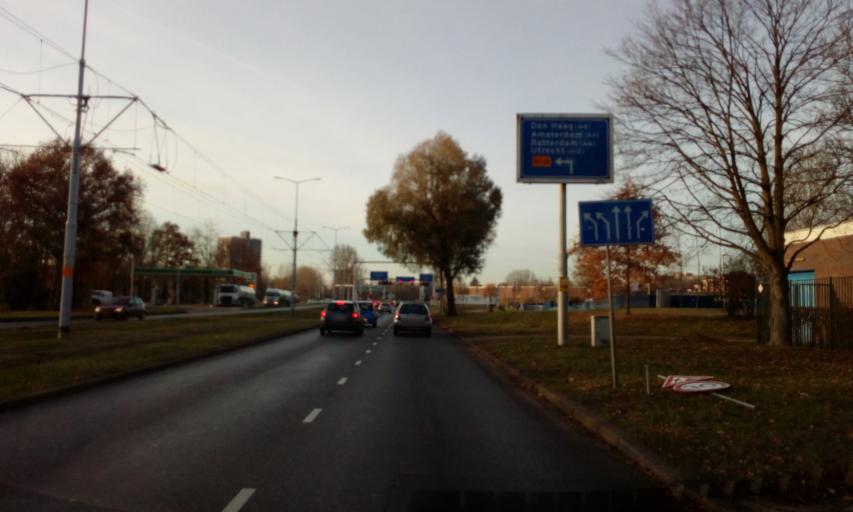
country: NL
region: South Holland
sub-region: Gemeente Leidschendam-Voorburg
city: Voorburg
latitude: 52.0863
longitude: 4.3821
